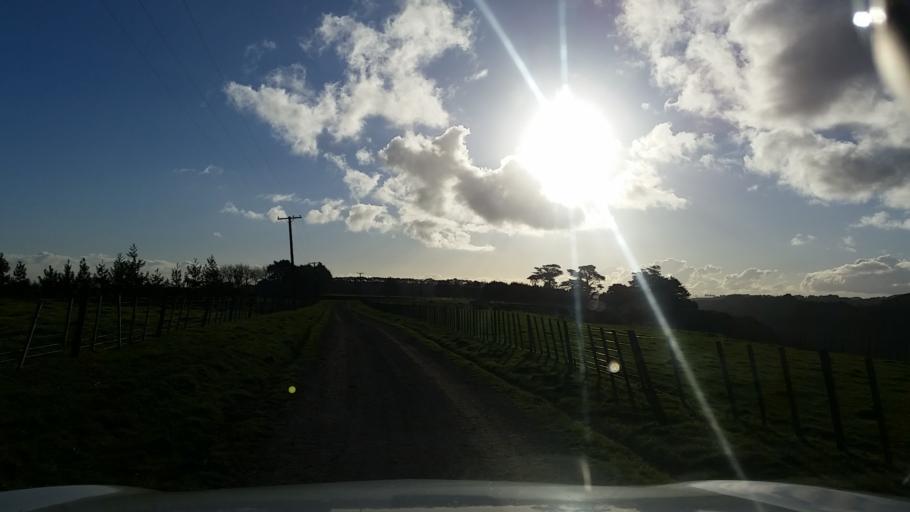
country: NZ
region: Taranaki
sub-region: South Taranaki District
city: Patea
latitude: -39.6170
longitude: 174.4970
